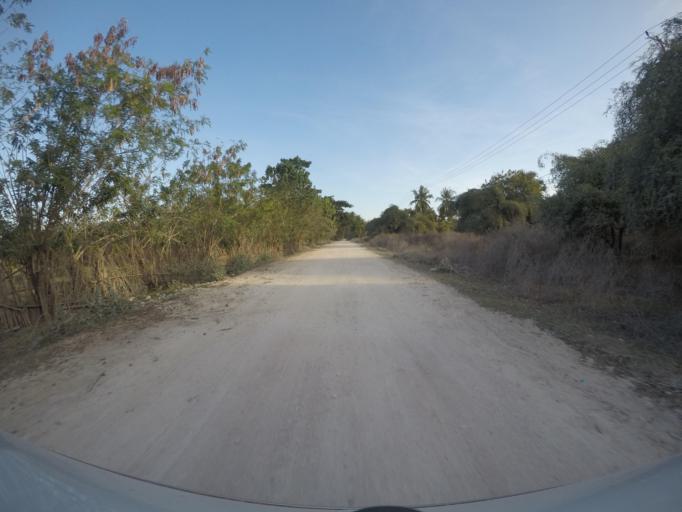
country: TL
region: Viqueque
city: Viqueque
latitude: -8.8783
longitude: 126.5076
